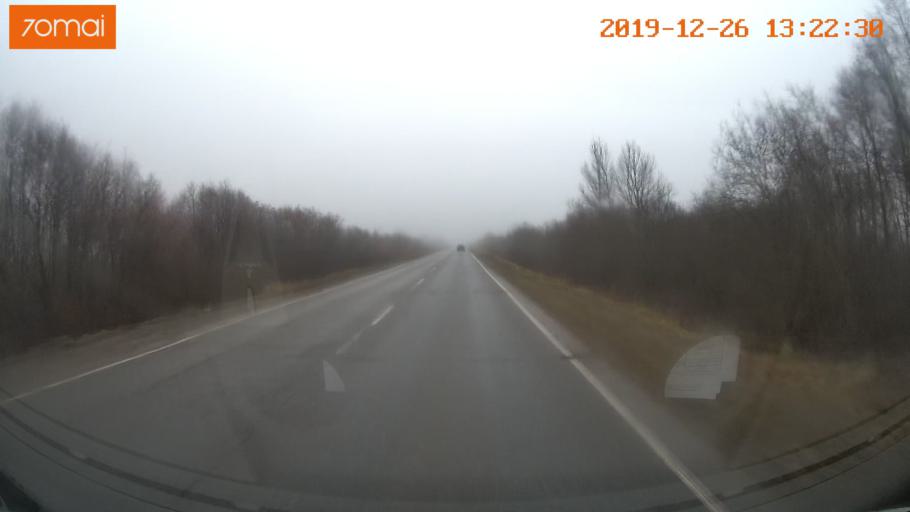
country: RU
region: Vologda
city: Cherepovets
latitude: 58.9011
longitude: 38.1729
